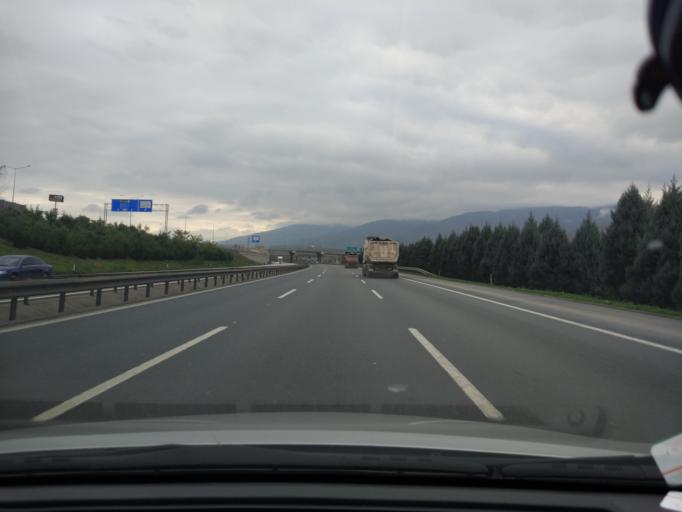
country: TR
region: Kocaeli
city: Kosekoy
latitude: 40.7342
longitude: 30.0525
